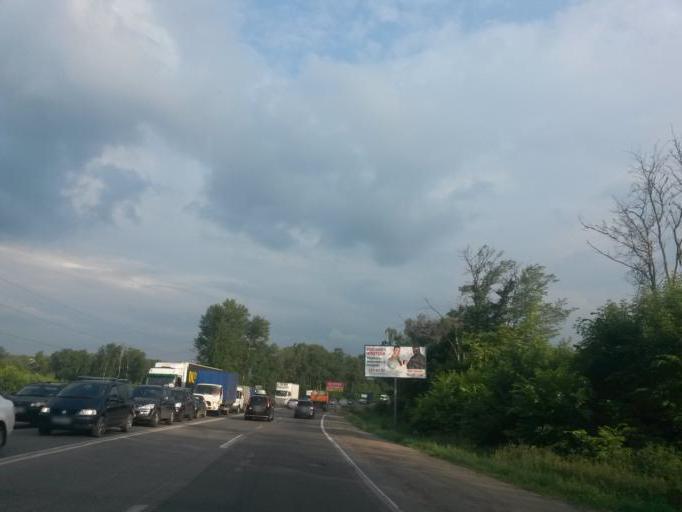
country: RU
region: Moskovskaya
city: Petrovskaya
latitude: 55.5587
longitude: 37.7740
